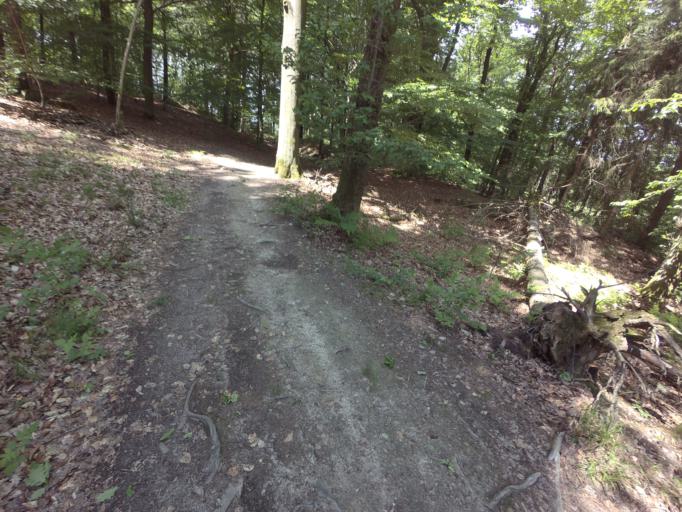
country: BE
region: Wallonia
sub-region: Province de Liege
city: Jalhay
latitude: 50.5188
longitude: 5.9736
